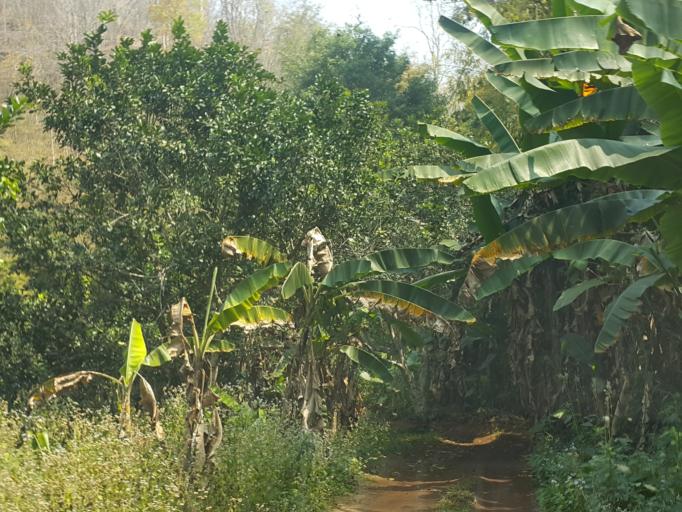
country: TH
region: Chiang Mai
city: Hang Dong
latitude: 18.7586
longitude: 98.8209
